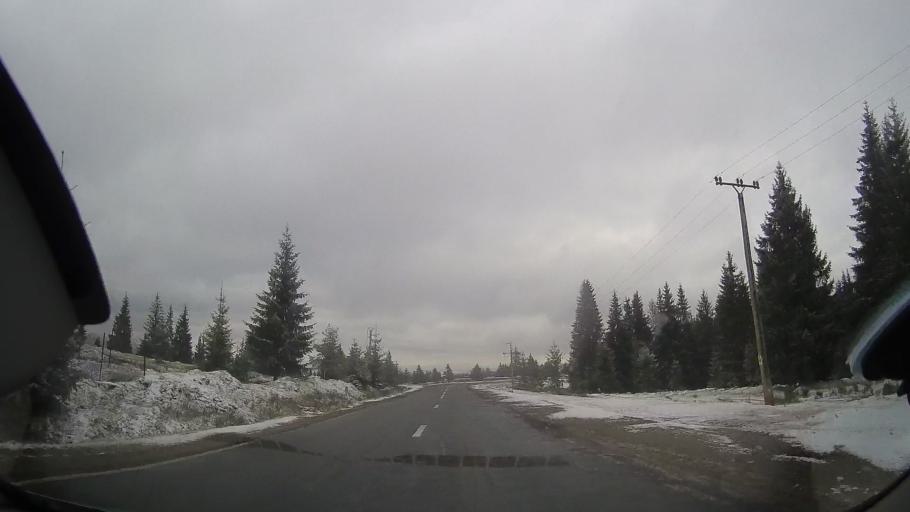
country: RO
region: Cluj
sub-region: Comuna Belis
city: Belis
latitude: 46.7002
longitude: 23.0363
